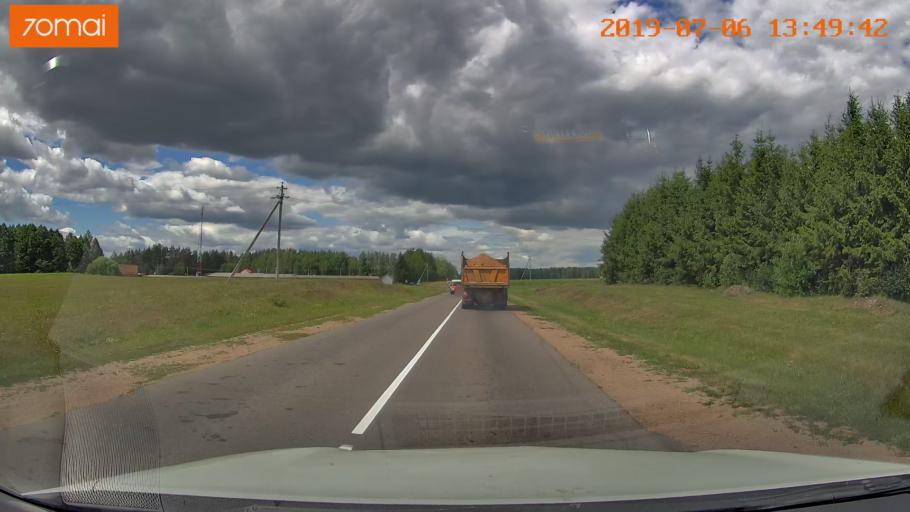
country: BY
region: Minsk
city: Ivyanyets
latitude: 53.6951
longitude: 26.8501
